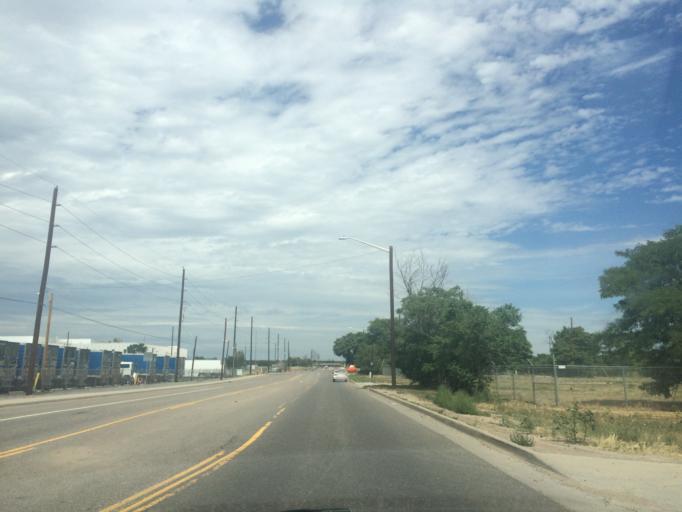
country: US
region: Colorado
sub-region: Adams County
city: Welby
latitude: 39.8165
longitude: -104.9592
